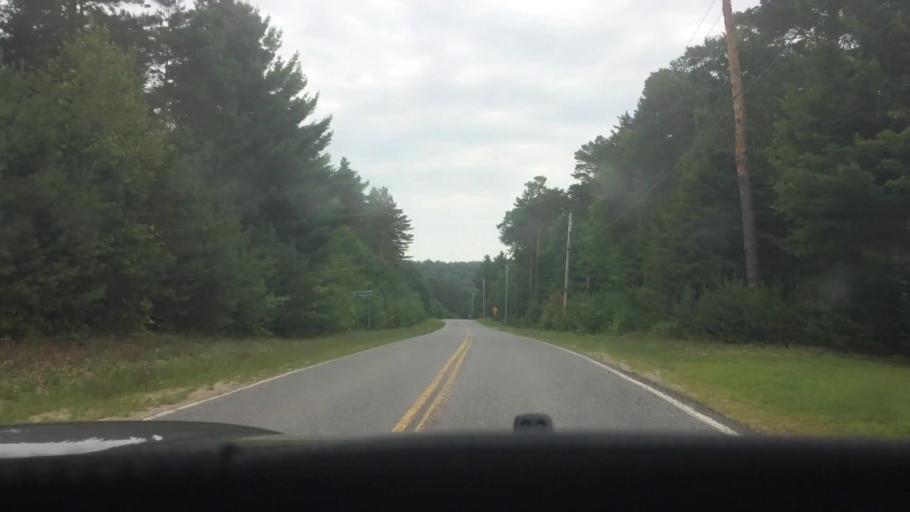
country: US
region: New York
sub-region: St. Lawrence County
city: Hannawa Falls
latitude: 44.5592
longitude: -74.9264
